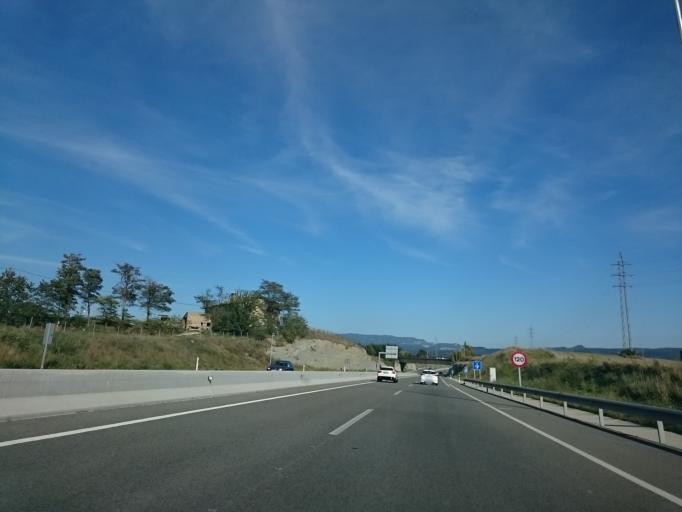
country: ES
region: Catalonia
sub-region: Provincia de Barcelona
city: Gurb
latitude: 41.9598
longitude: 2.2556
